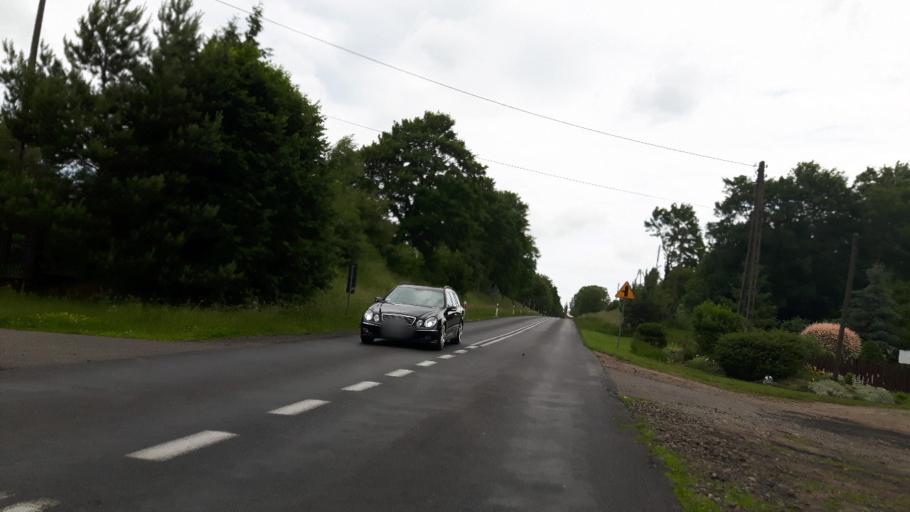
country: PL
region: West Pomeranian Voivodeship
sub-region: Powiat gryficki
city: Gryfice
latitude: 53.9694
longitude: 15.2324
